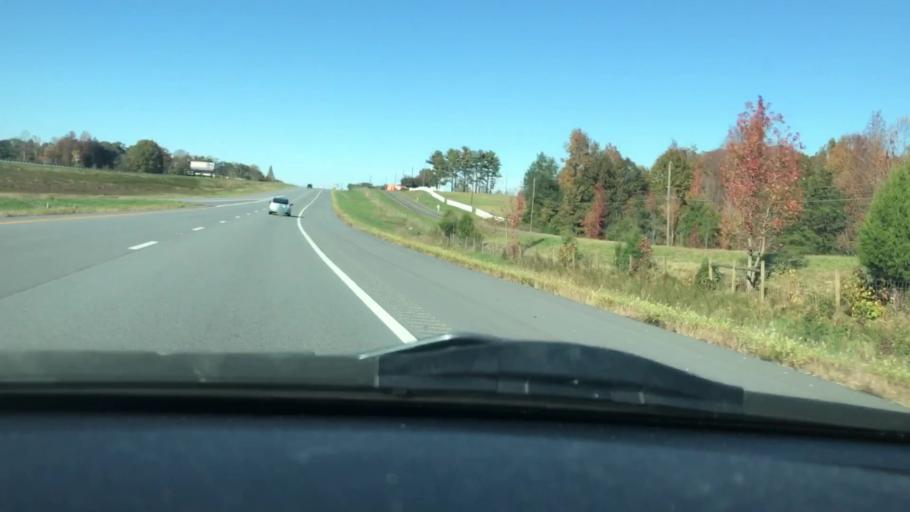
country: US
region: North Carolina
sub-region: Guilford County
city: Stokesdale
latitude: 36.2853
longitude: -79.9395
